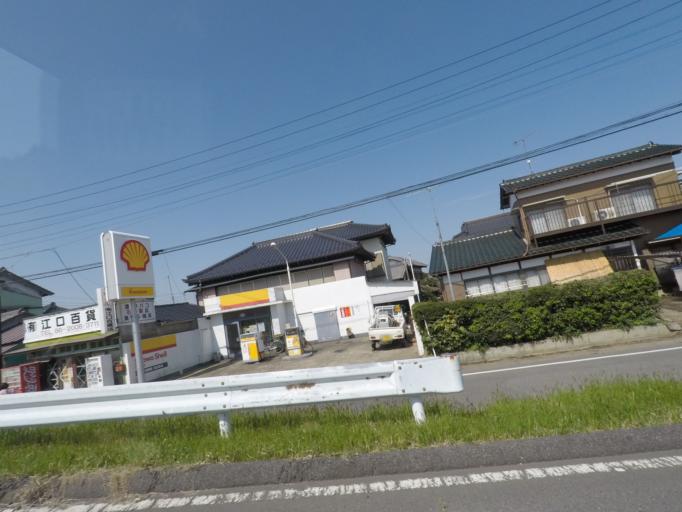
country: JP
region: Ibaraki
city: Edosaki
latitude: 35.8854
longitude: 140.3473
